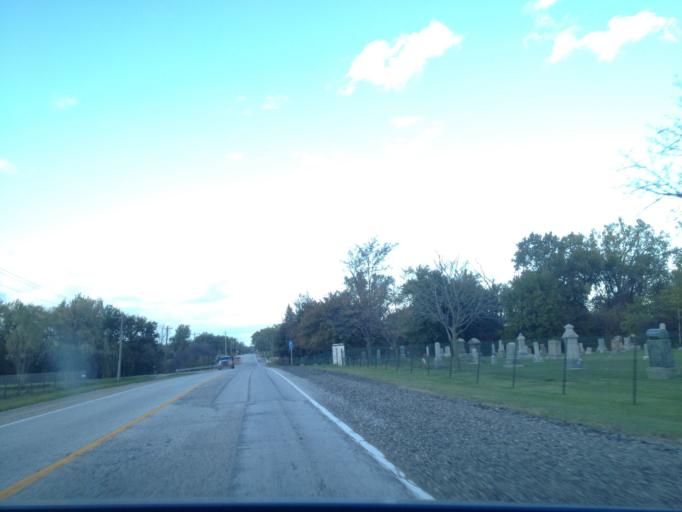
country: US
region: Michigan
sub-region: Wayne County
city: Grosse Pointe
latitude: 42.1762
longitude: -82.7203
